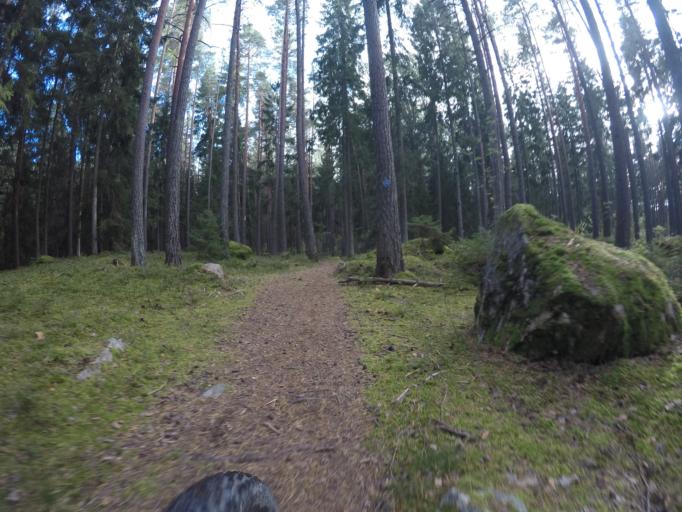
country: SE
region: Vaestmanland
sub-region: Kopings Kommun
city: Koping
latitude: 59.5297
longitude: 16.0008
